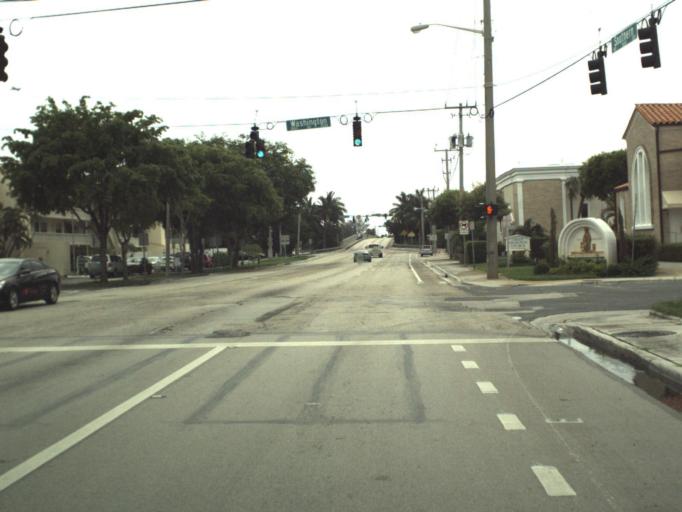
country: US
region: Florida
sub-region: Palm Beach County
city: Palm Beach
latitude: 26.6755
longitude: -80.0504
